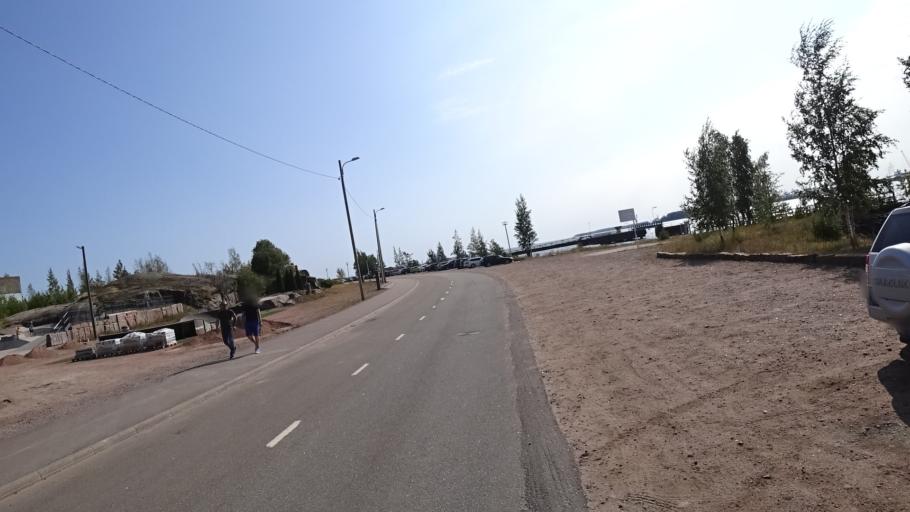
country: FI
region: Kymenlaakso
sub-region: Kotka-Hamina
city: Kotka
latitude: 60.4498
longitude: 26.9339
